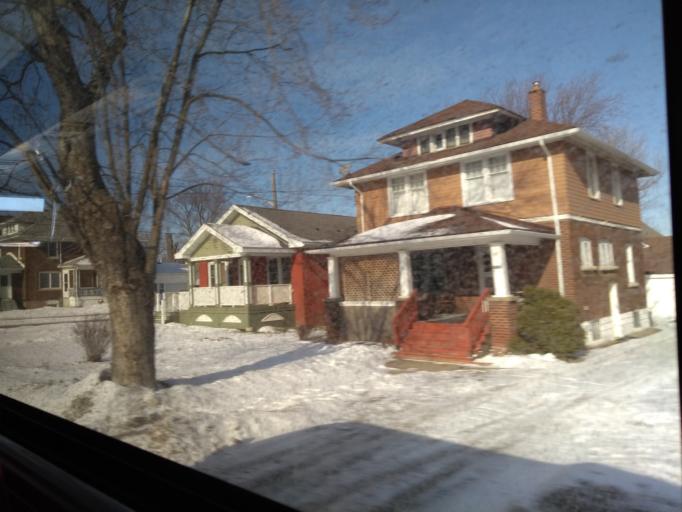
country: CA
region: Ontario
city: Niagara Falls
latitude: 43.1086
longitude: -79.0794
